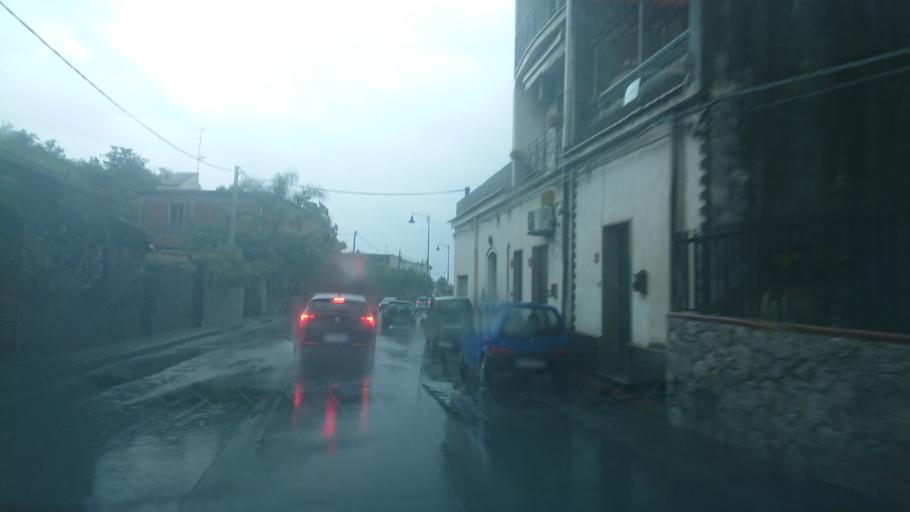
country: IT
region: Sicily
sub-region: Catania
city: Pasteria-Lapide
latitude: 37.8062
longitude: 15.2242
